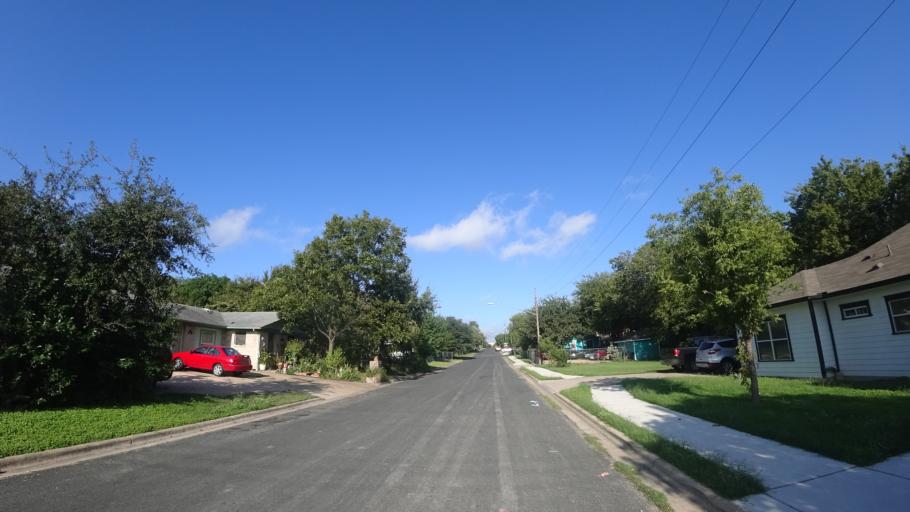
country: US
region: Texas
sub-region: Travis County
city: Austin
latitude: 30.3299
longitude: -97.6945
